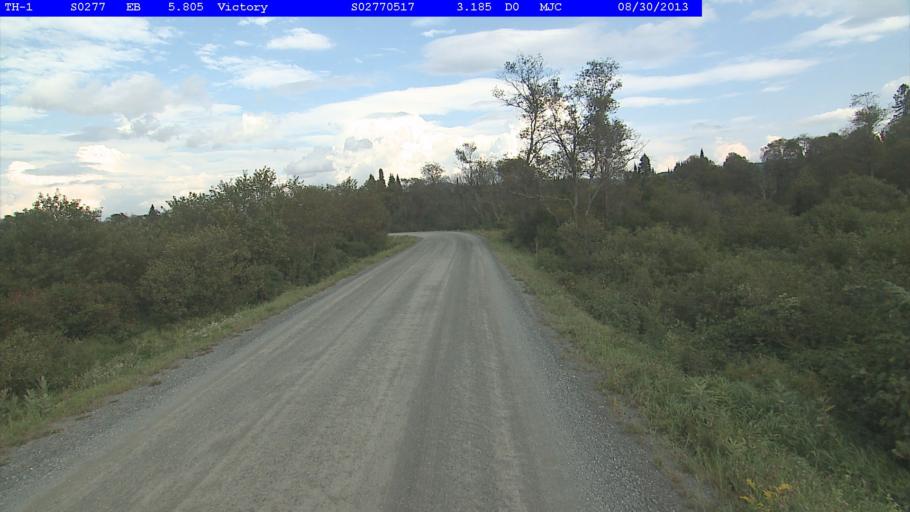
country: US
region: Vermont
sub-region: Caledonia County
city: Lyndonville
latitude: 44.5276
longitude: -71.8136
